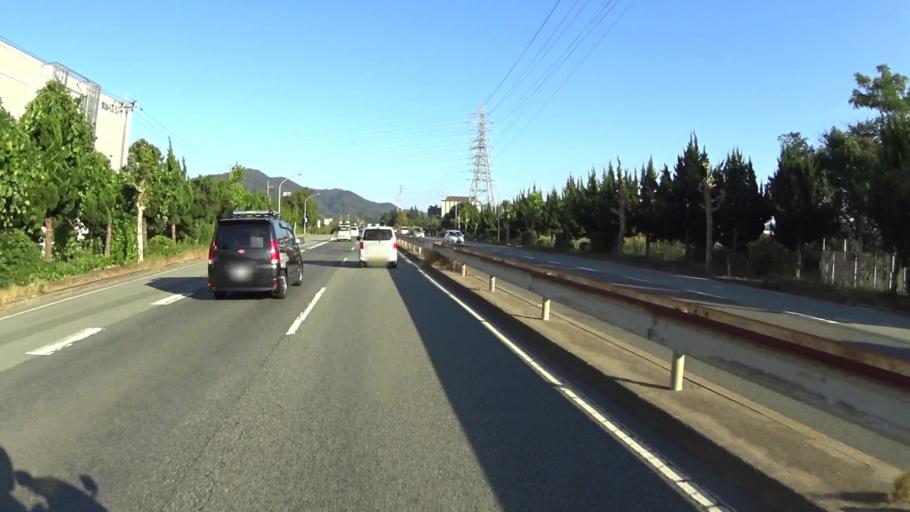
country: JP
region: Kyoto
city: Fukuchiyama
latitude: 35.2888
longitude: 135.1695
